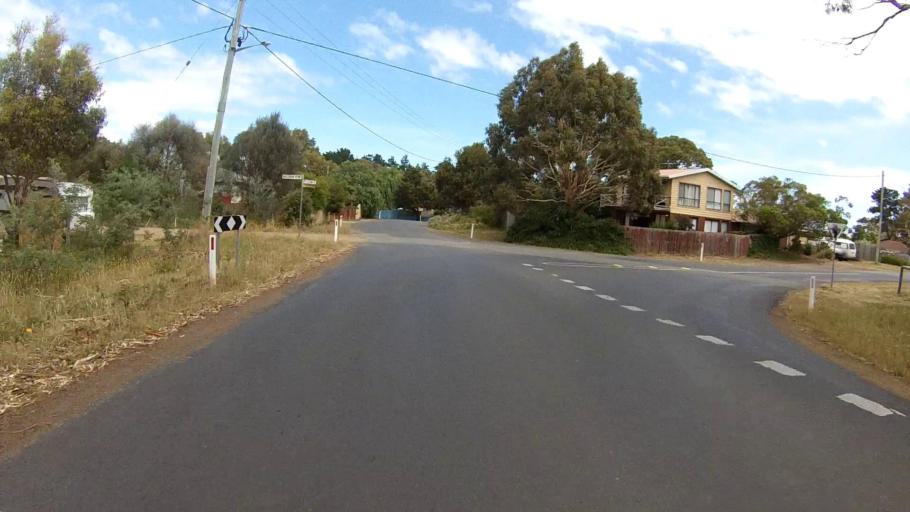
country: AU
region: Tasmania
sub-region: Sorell
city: Sorell
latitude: -42.8705
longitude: 147.6425
